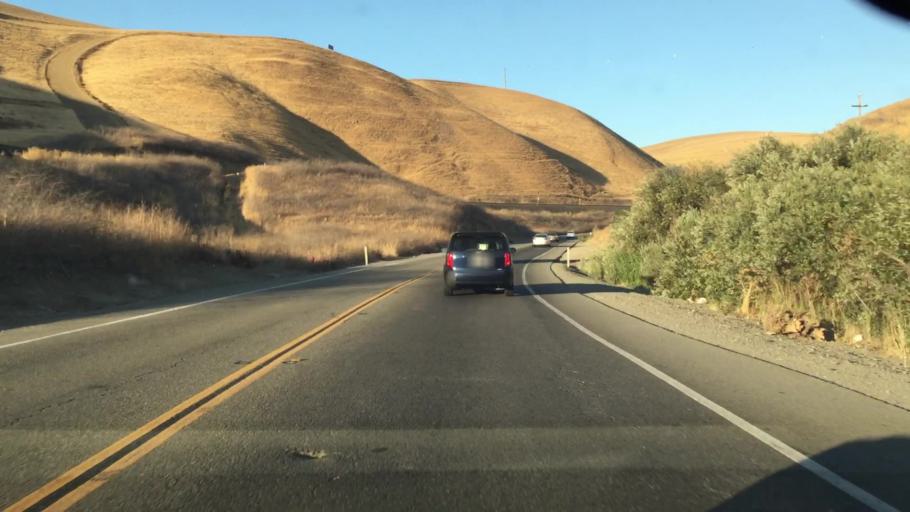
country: US
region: California
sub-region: Alameda County
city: Livermore
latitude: 37.7230
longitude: -121.6864
